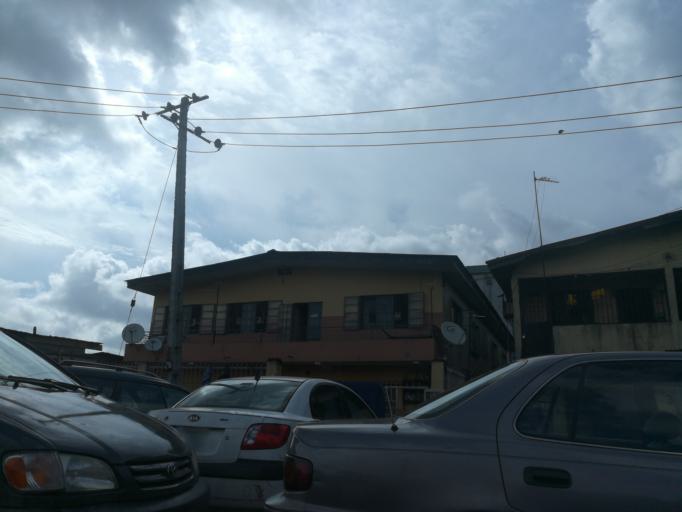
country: NG
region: Lagos
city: Somolu
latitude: 6.5473
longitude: 3.3749
